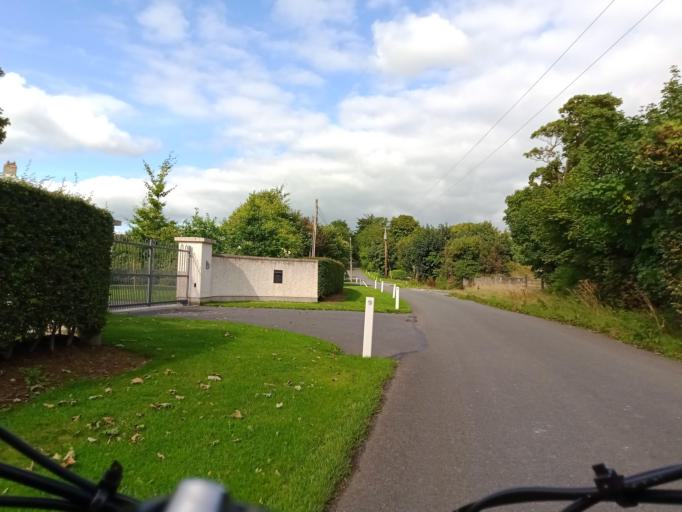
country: IE
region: Leinster
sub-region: Kilkenny
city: Kilkenny
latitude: 52.6133
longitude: -7.2110
